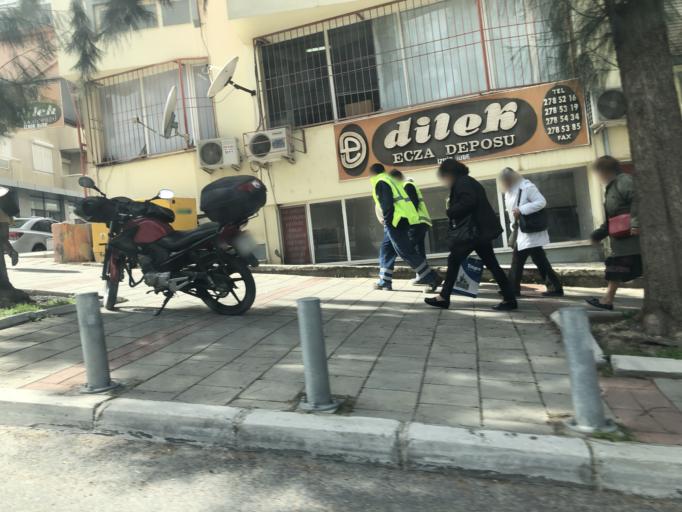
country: TR
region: Izmir
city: Karsiyaka
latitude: 38.3929
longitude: 27.0447
